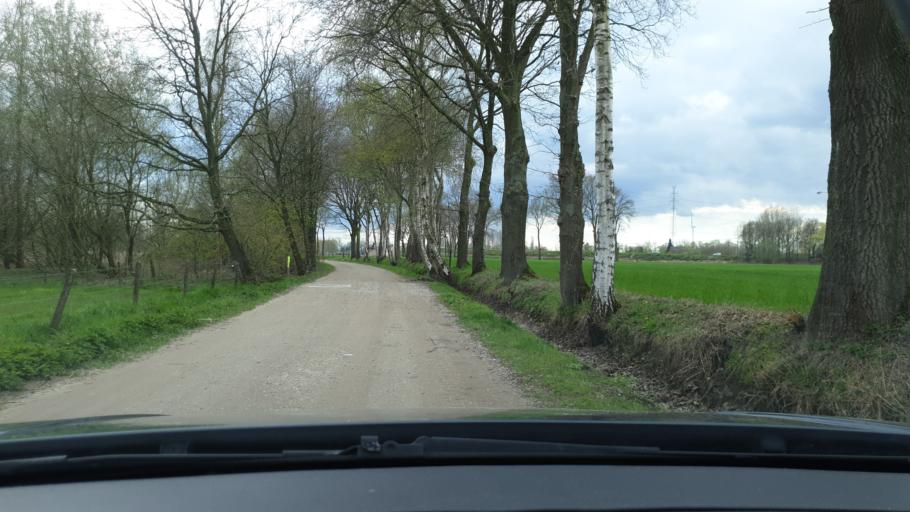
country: BE
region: Flanders
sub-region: Provincie Antwerpen
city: Geel
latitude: 51.1299
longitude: 4.9876
